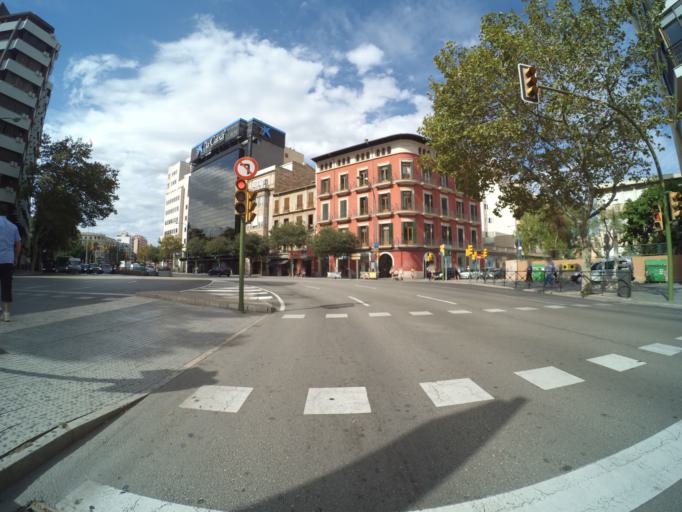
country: ES
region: Balearic Islands
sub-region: Illes Balears
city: Palma
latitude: 39.5749
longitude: 2.6555
